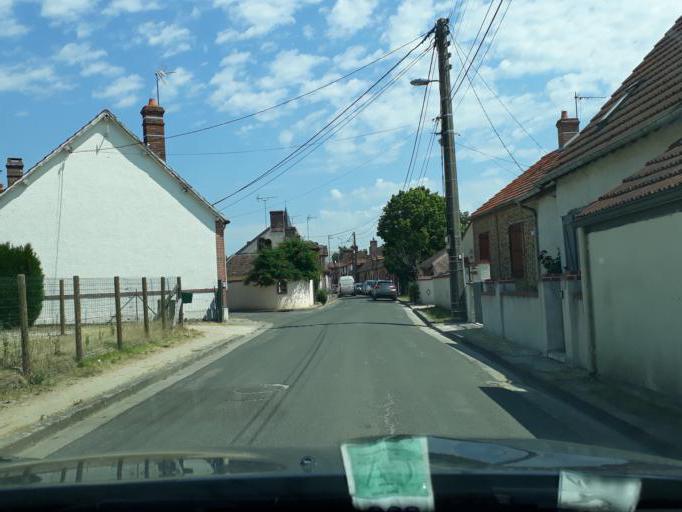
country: FR
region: Centre
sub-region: Departement du Loir-et-Cher
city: Vouzon
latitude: 47.6437
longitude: 2.0556
